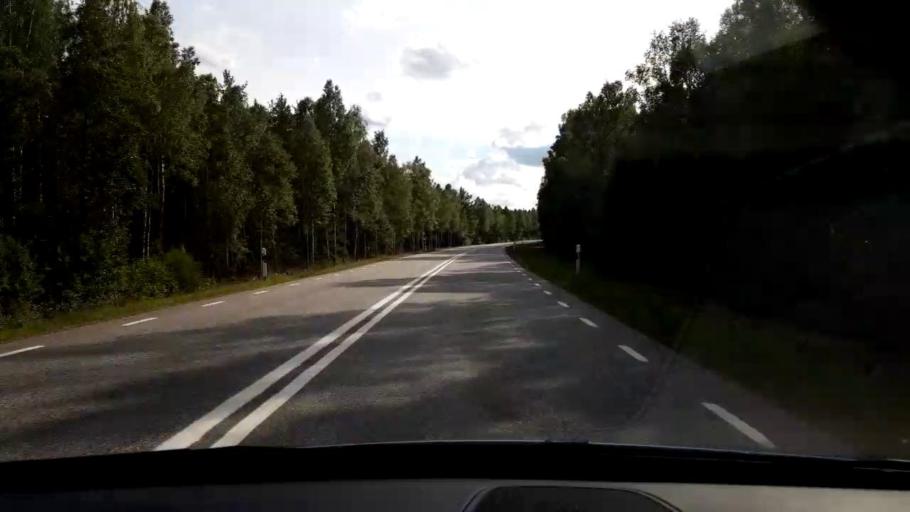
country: SE
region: Joenkoeping
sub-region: Savsjo Kommun
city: Vrigstad
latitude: 57.2946
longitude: 14.3010
